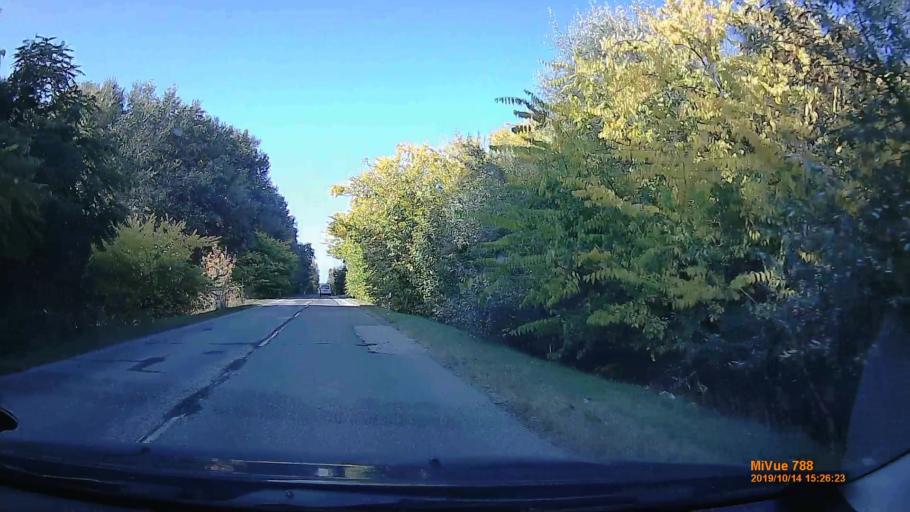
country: HU
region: Pest
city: Ecser
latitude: 47.4183
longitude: 19.3144
